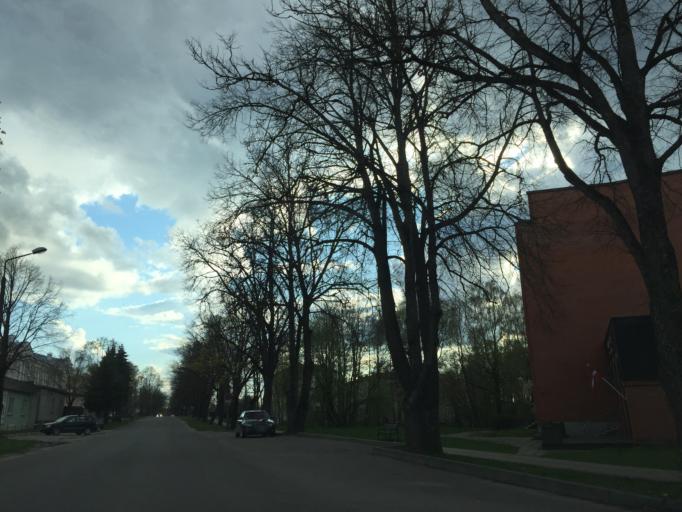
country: LV
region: Cesu Rajons
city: Cesis
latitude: 57.3191
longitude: 25.2868
